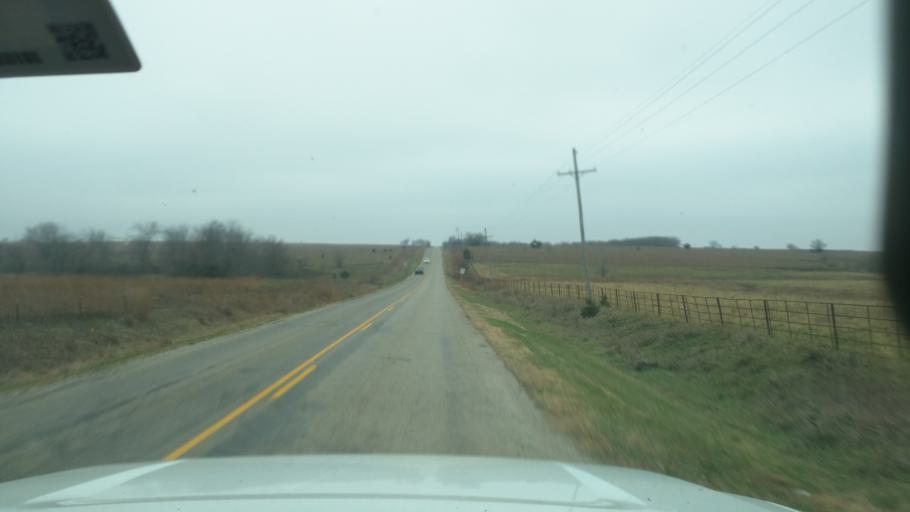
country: US
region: Kansas
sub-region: Lyon County
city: Emporia
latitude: 38.5887
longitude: -96.2610
